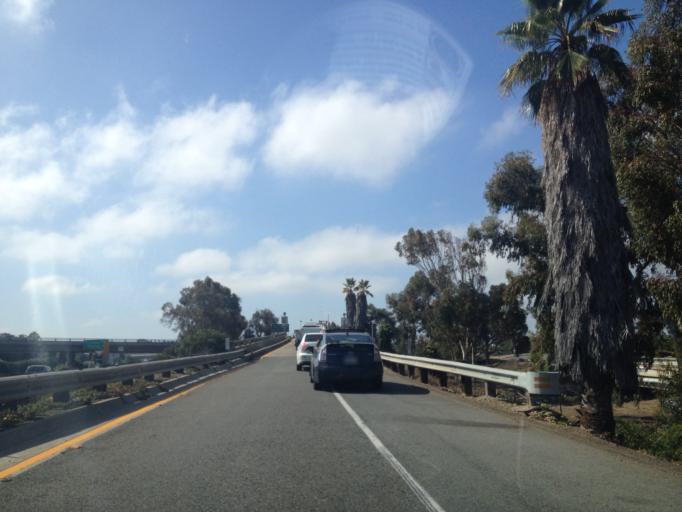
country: US
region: California
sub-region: San Diego County
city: San Diego
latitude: 32.7715
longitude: -117.2074
